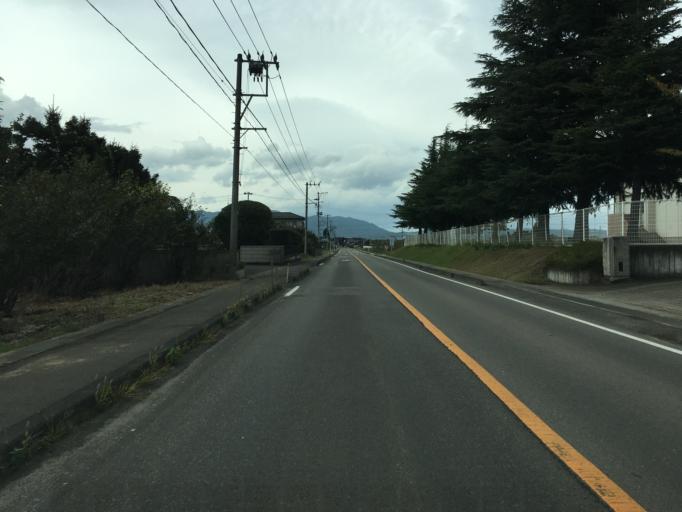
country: JP
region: Fukushima
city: Hobaramachi
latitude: 37.8327
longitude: 140.5580
